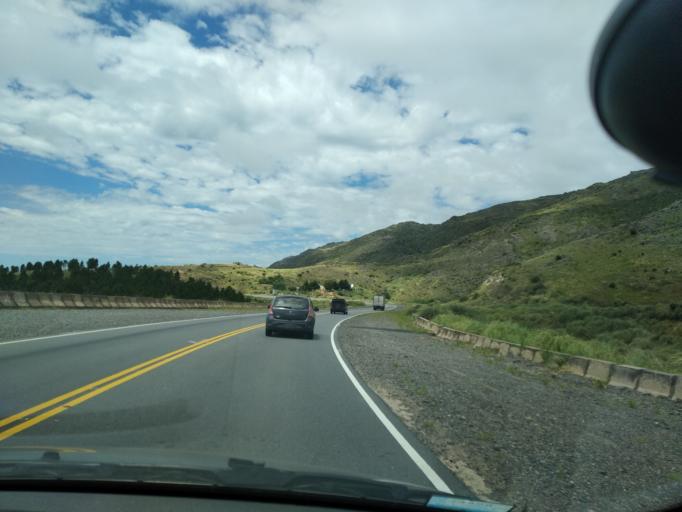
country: AR
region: Cordoba
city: Cuesta Blanca
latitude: -31.6169
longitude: -64.6869
